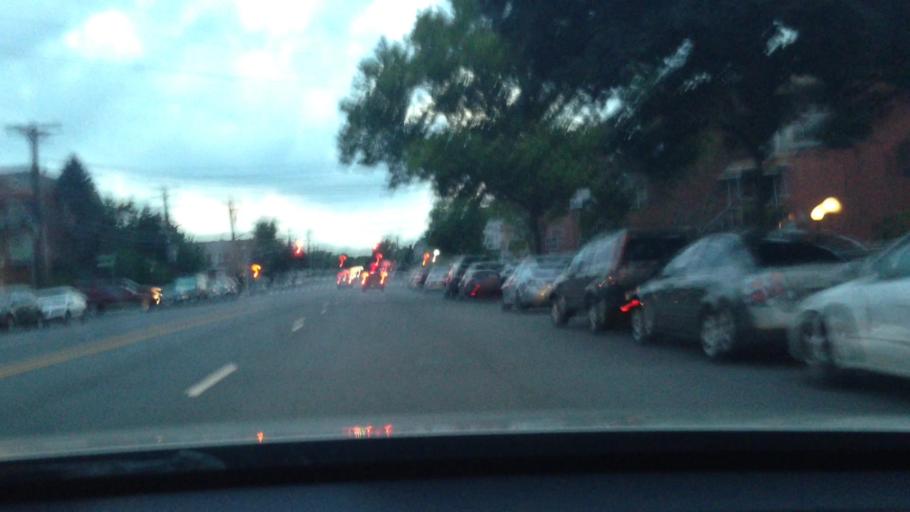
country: US
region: New York
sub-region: Kings County
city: East New York
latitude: 40.6291
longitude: -73.9034
